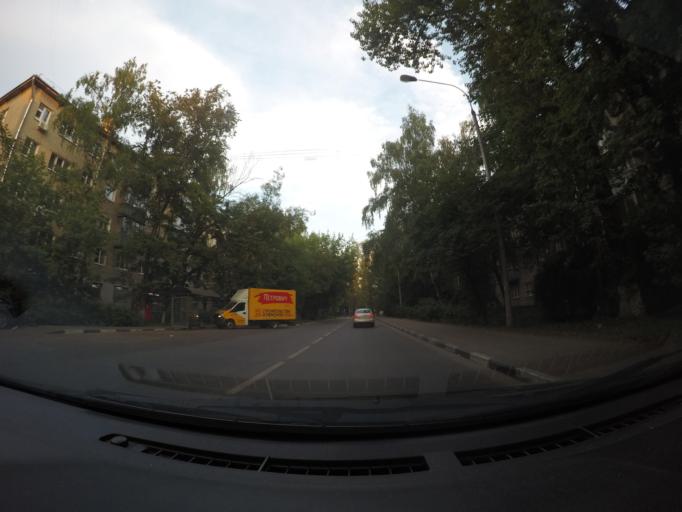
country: RU
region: Moskovskaya
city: Lyubertsy
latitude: 55.6588
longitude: 37.9074
